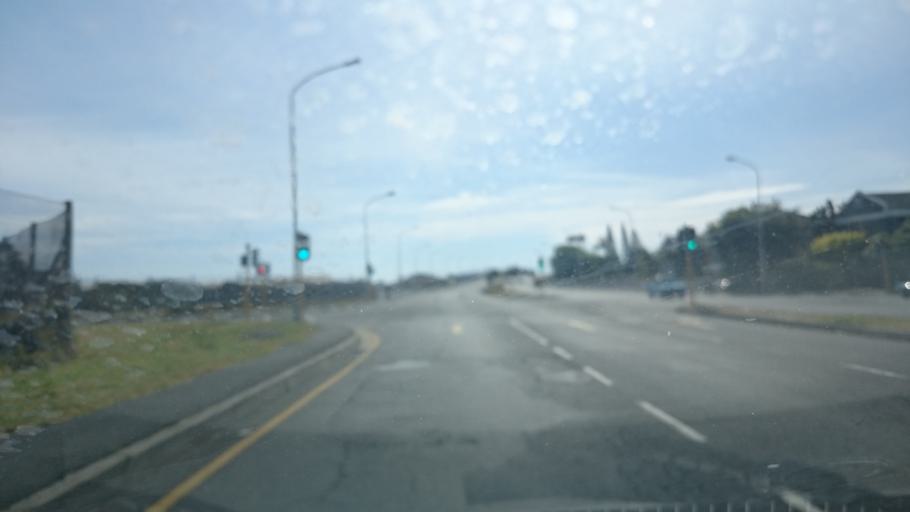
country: ZA
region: Western Cape
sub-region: City of Cape Town
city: Lansdowne
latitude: -34.0123
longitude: 18.4917
